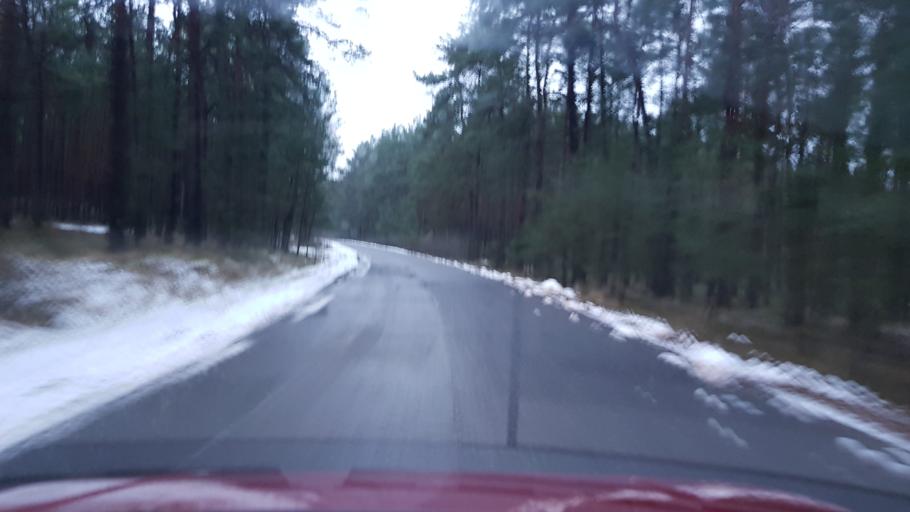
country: PL
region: West Pomeranian Voivodeship
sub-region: Powiat goleniowski
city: Goleniow
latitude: 53.4745
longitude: 14.8328
